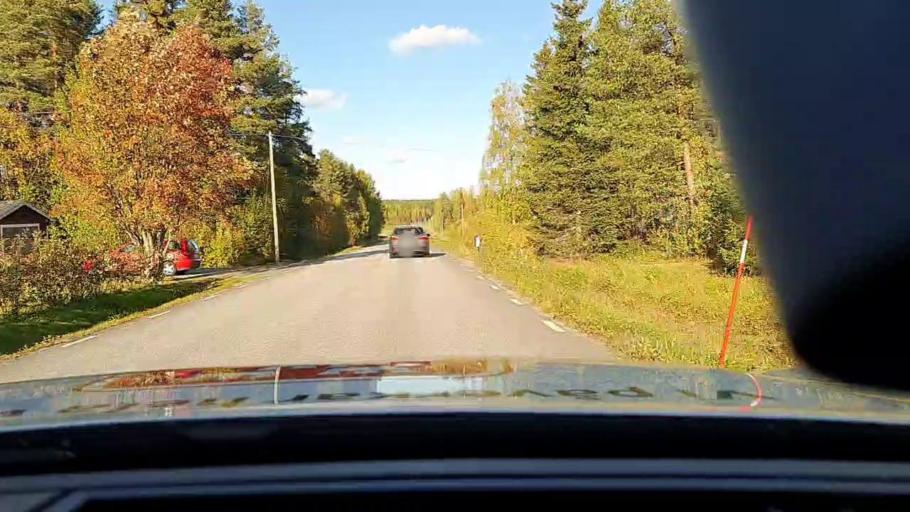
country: SE
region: Norrbotten
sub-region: Pitea Kommun
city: Norrfjarden
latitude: 65.5091
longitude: 21.4867
